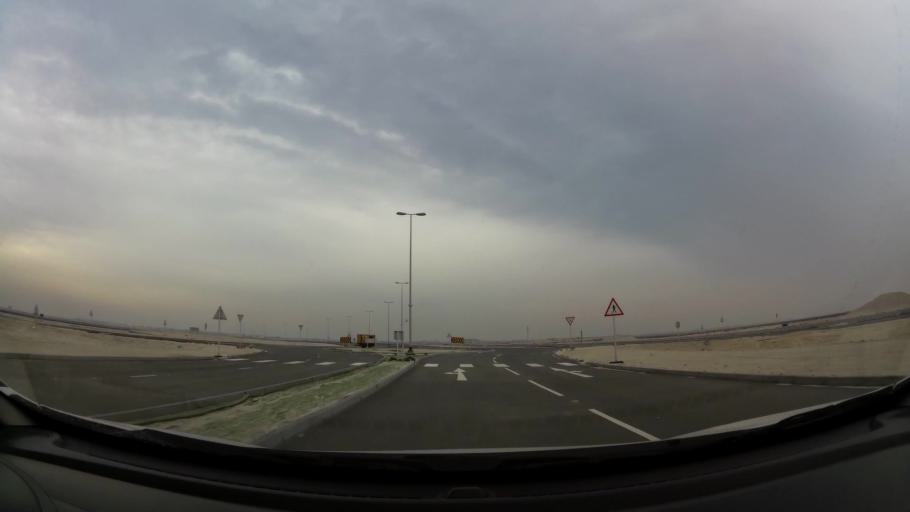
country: BH
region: Central Governorate
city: Dar Kulayb
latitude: 25.8652
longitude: 50.6050
